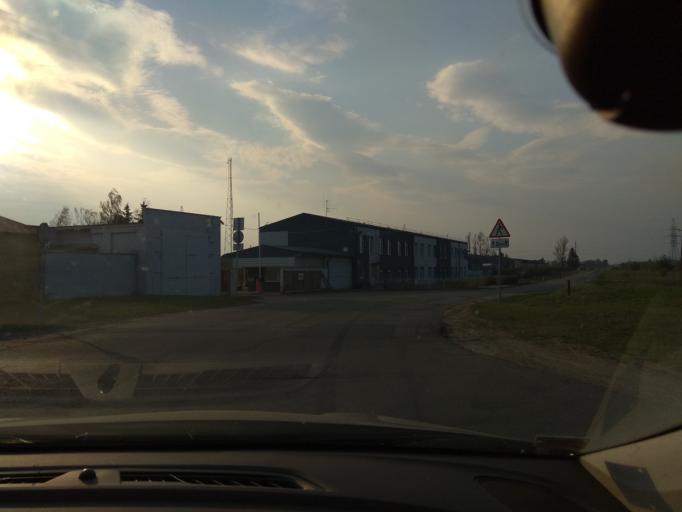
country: LT
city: Baltoji Voke
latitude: 54.6113
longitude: 25.1216
